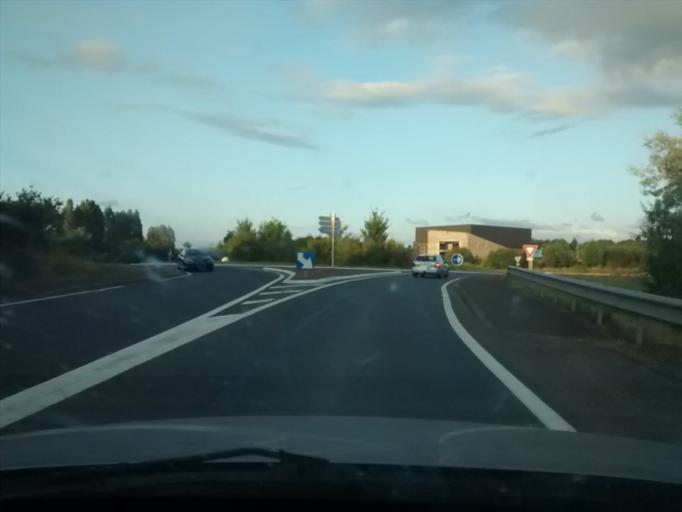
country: FR
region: Pays de la Loire
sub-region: Departement de la Sarthe
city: Saint-Saturnin
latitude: 48.0680
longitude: 0.1678
